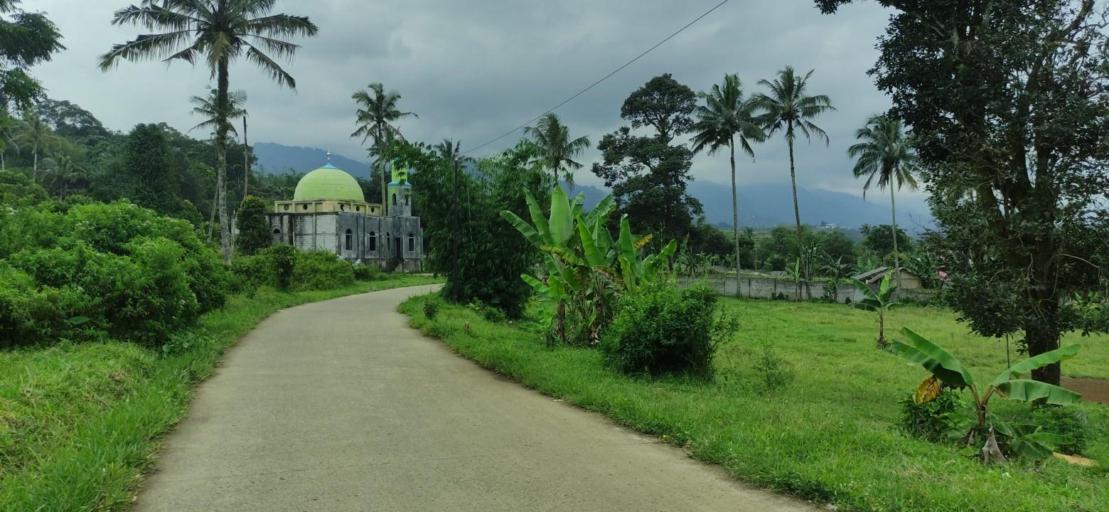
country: ID
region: West Java
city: Caringin
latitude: -6.6419
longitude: 106.8906
